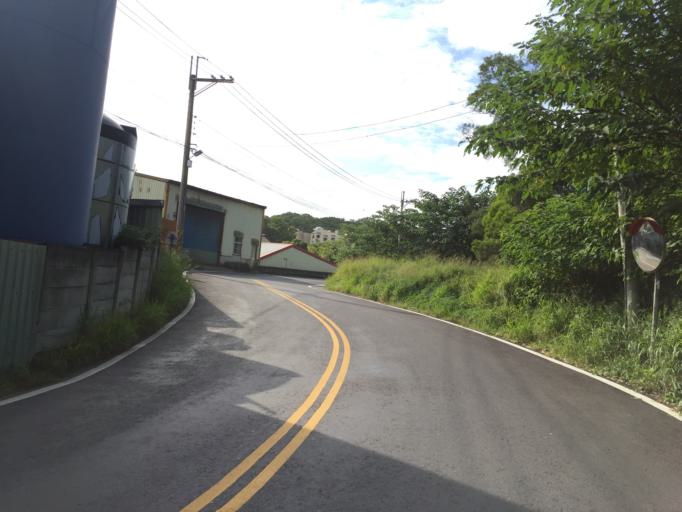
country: TW
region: Taiwan
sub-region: Hsinchu
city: Hsinchu
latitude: 24.7746
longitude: 120.9326
